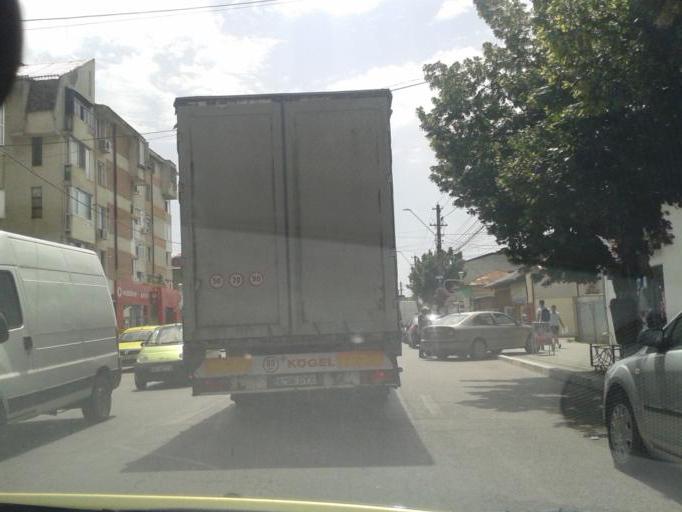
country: RO
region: Dambovita
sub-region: Oras Gaesti
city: Gaesti
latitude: 44.7193
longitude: 25.3218
